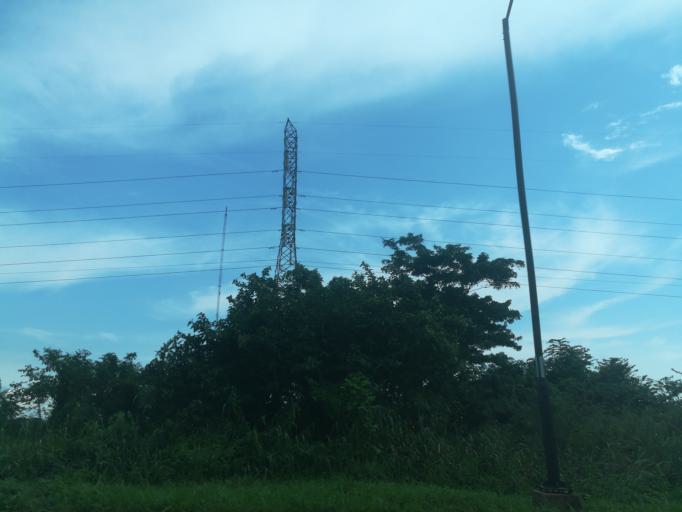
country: NG
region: Lagos
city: Ikorodu
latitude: 6.6354
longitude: 3.5260
